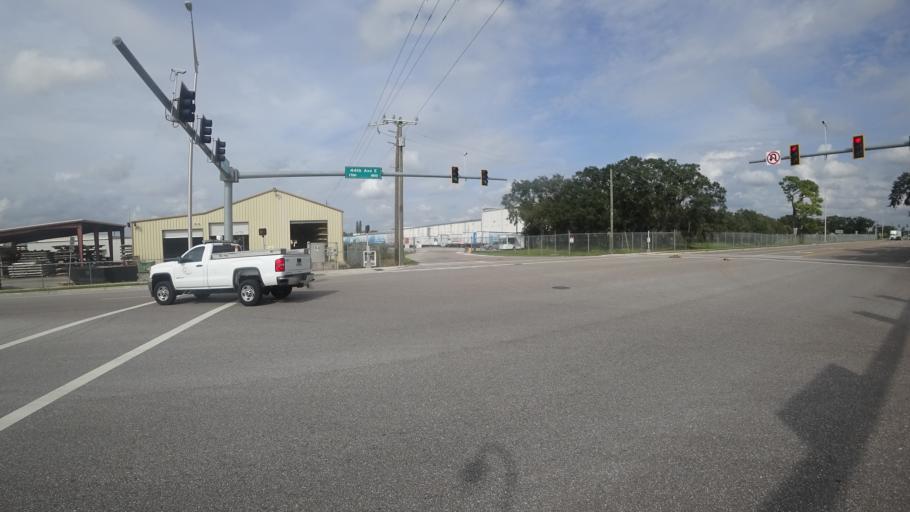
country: US
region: Florida
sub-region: Manatee County
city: Samoset
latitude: 27.4621
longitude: -82.5426
